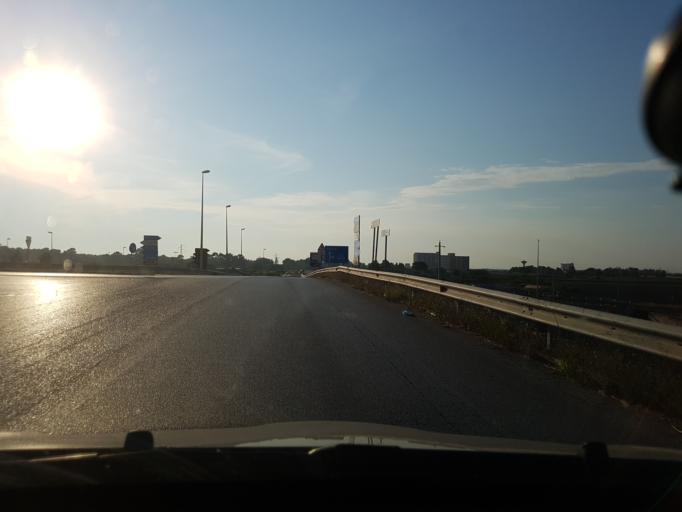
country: IT
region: Apulia
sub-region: Provincia di Foggia
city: Carapelle
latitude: 41.3946
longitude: 15.6612
